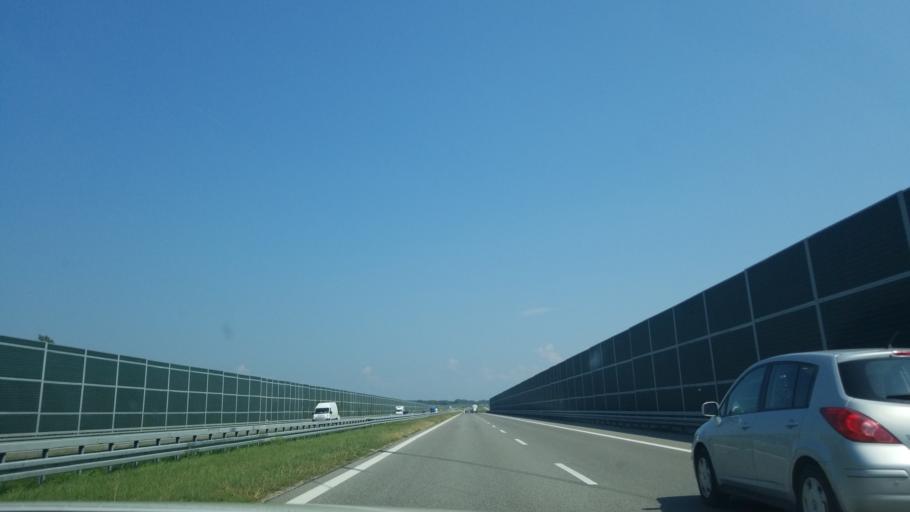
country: PL
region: Subcarpathian Voivodeship
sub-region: Powiat ropczycko-sedziszowski
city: Sedziszow Malopolski
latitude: 50.1102
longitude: 21.6899
